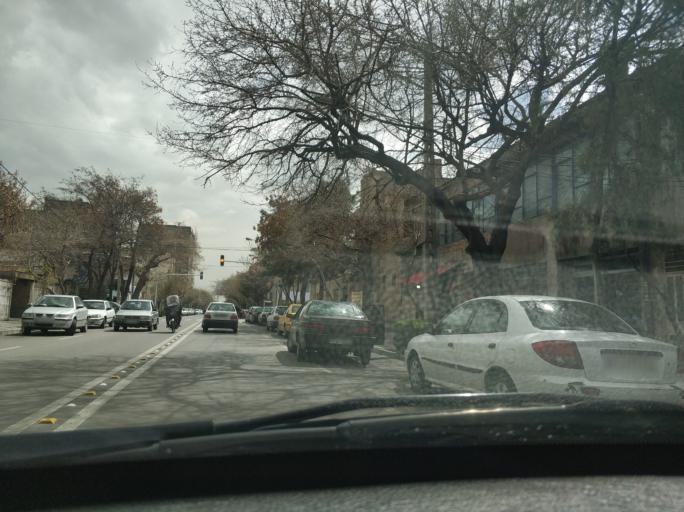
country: IR
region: Razavi Khorasan
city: Mashhad
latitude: 36.2809
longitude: 59.5733
